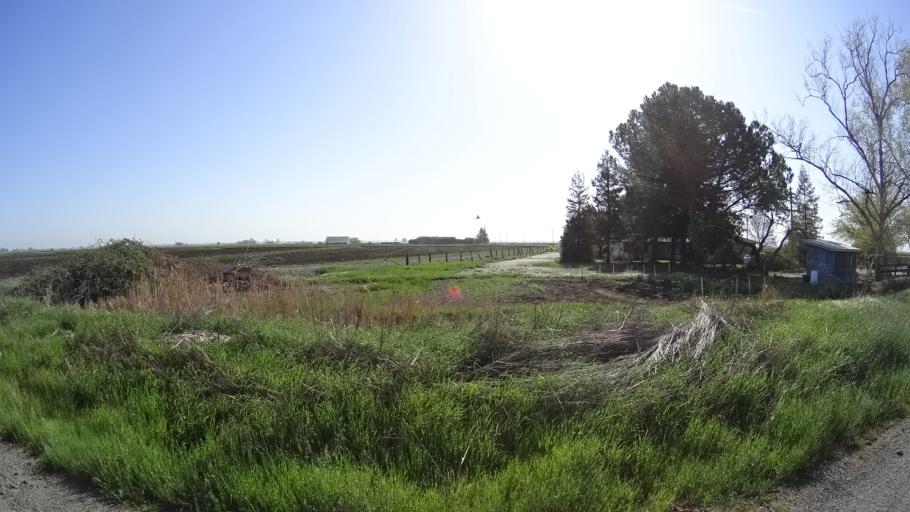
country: US
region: California
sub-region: Glenn County
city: Willows
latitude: 39.5587
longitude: -122.0839
